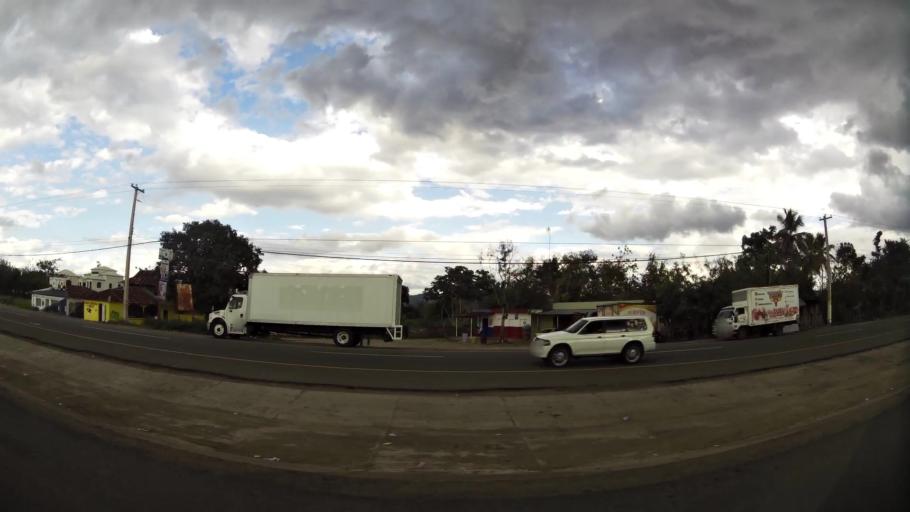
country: DO
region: Monsenor Nouel
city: Sabana del Puerto
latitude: 19.0487
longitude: -70.4460
